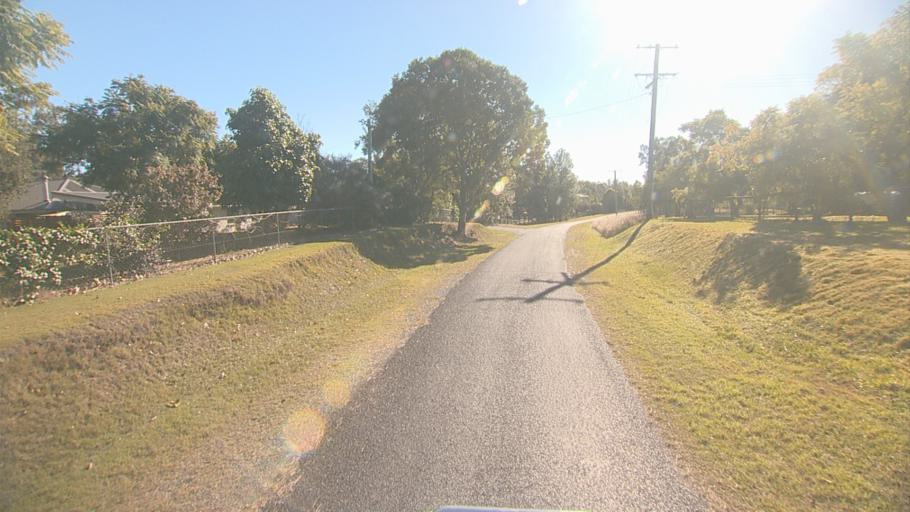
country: AU
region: Queensland
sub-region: Logan
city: Chambers Flat
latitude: -27.7569
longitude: 153.0539
